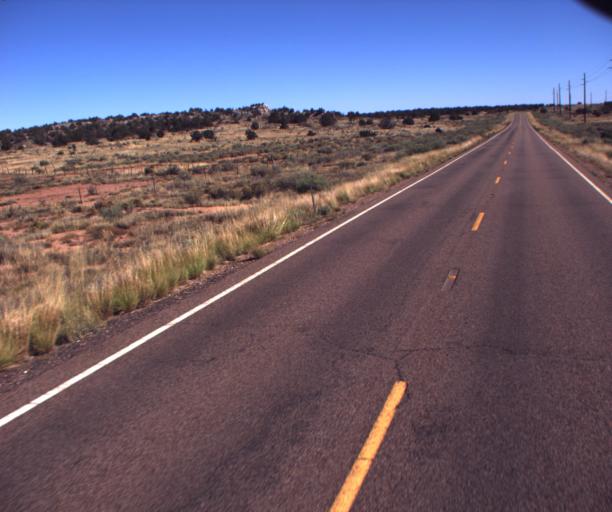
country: US
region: Arizona
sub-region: Navajo County
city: Taylor
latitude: 34.5058
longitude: -110.1853
